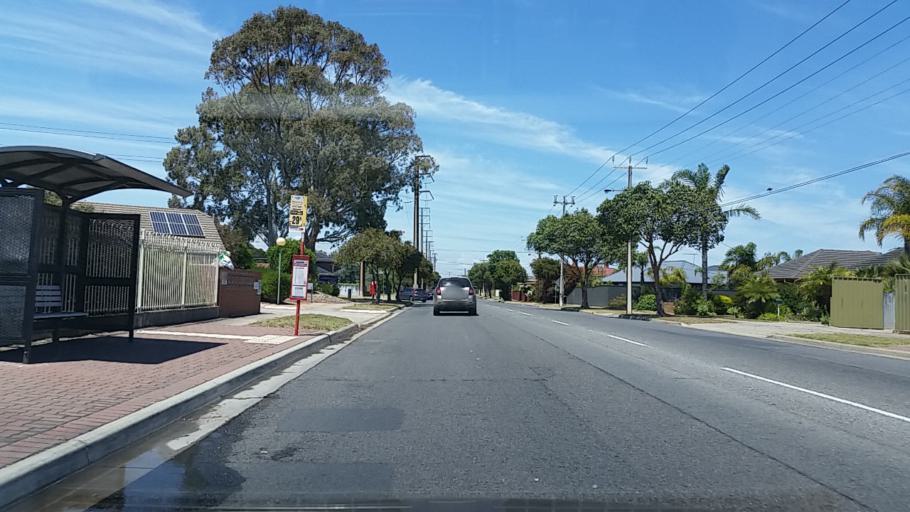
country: AU
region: South Australia
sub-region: Charles Sturt
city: Grange
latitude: -34.9020
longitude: 138.5053
